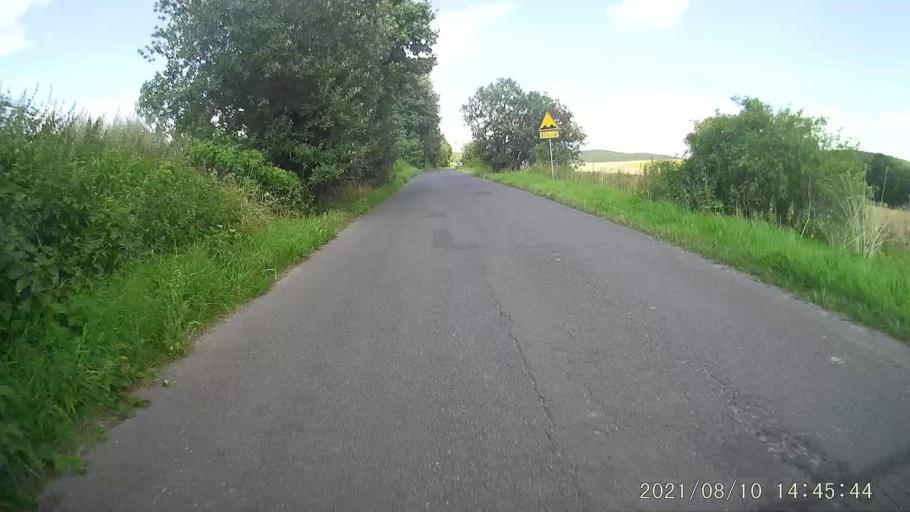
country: PL
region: Lower Silesian Voivodeship
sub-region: Powiat klodzki
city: Radkow
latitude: 50.5323
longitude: 16.4159
